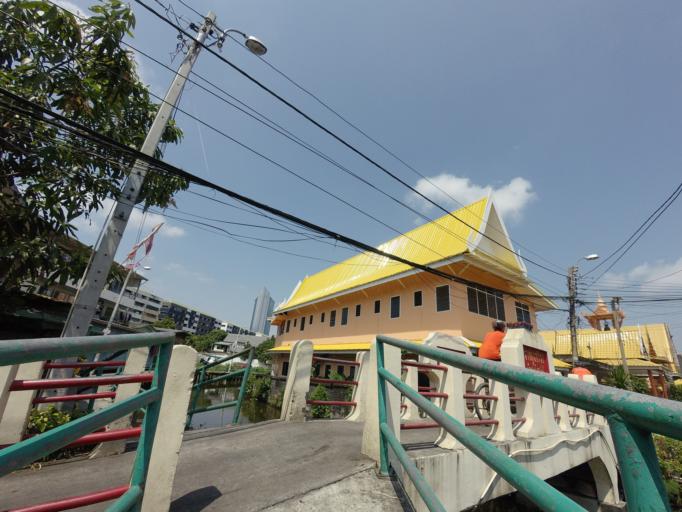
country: TH
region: Bangkok
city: Rat Burana
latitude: 13.6731
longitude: 100.5128
